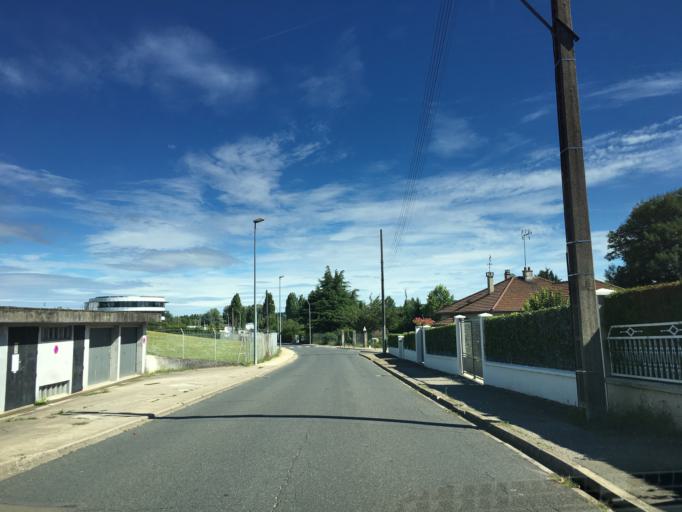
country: FR
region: Bourgogne
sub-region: Departement de l'Yonne
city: Auxerre
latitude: 47.8117
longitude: 3.5756
